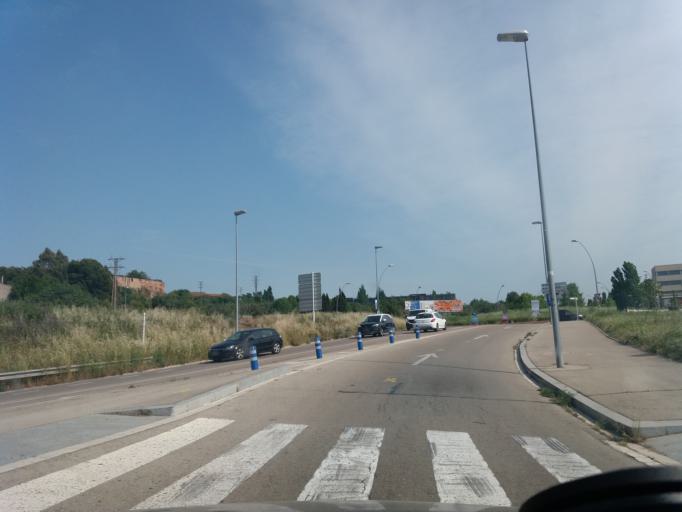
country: ES
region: Catalonia
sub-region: Provincia de Barcelona
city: Manresa
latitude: 41.7400
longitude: 1.8217
